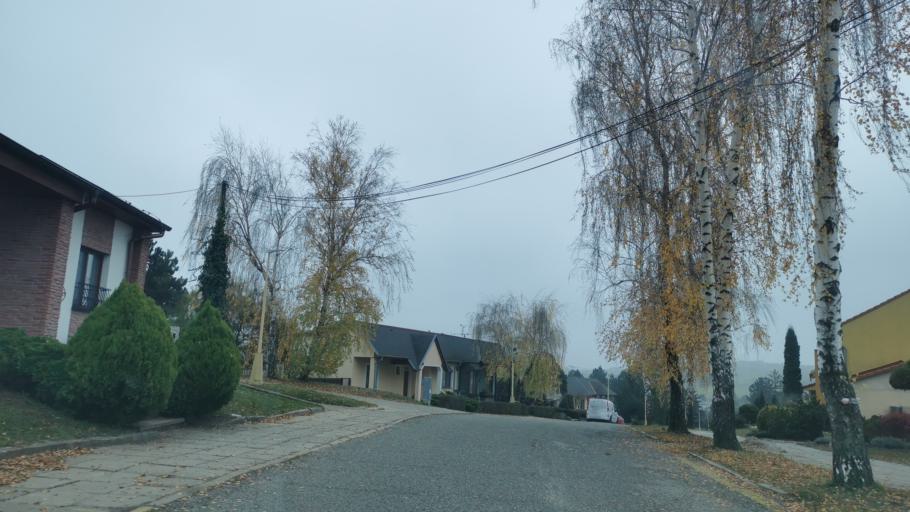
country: SK
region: Trnavsky
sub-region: Okres Skalica
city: Holic
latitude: 48.8151
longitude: 17.1702
